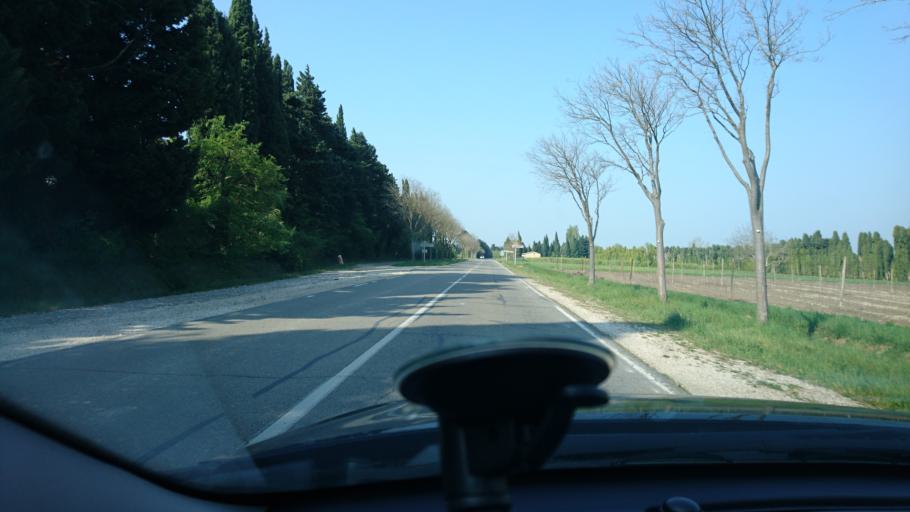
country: FR
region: Provence-Alpes-Cote d'Azur
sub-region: Departement des Bouches-du-Rhone
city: Saint-Andiol
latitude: 43.8391
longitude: 4.9156
